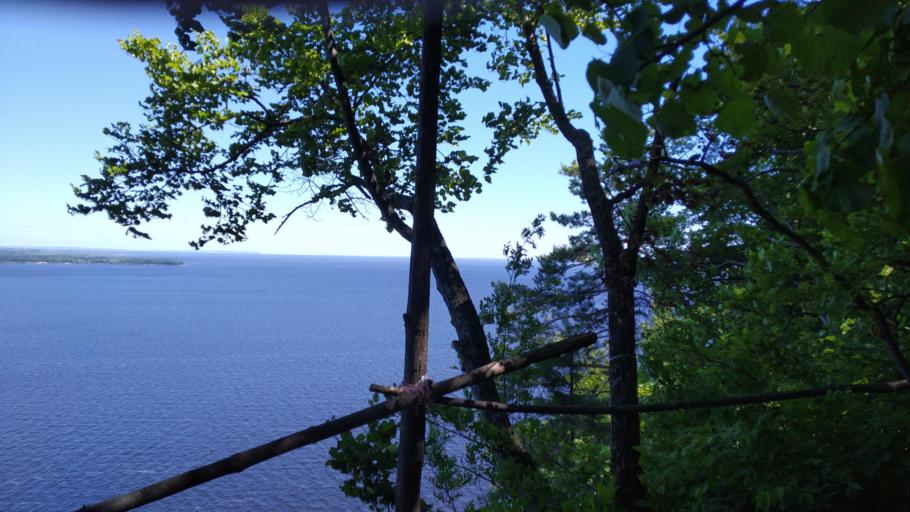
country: RU
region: Tatarstan
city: Kuybyshevskiy Zaton
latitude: 55.2350
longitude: 49.2294
